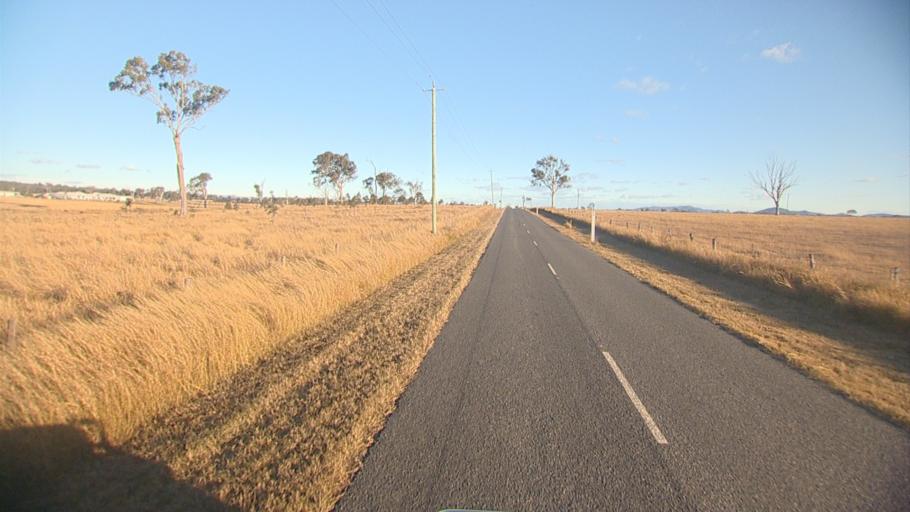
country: AU
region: Queensland
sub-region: Logan
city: Cedar Vale
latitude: -27.8680
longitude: 152.9576
